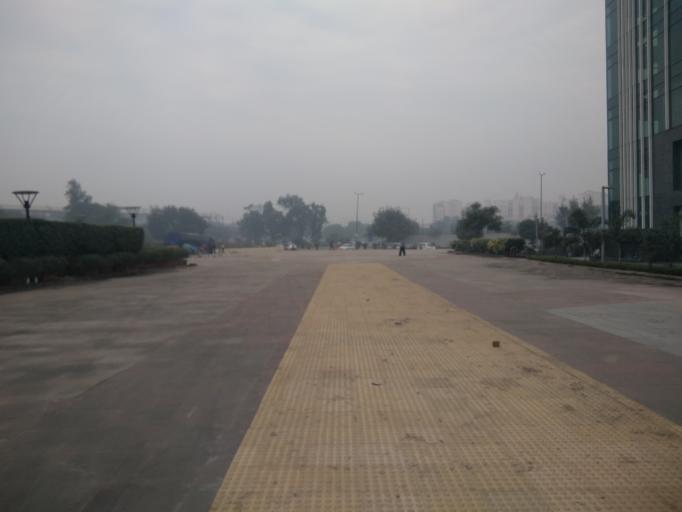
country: IN
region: Uttar Pradesh
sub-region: Gautam Buddha Nagar
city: Noida
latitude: 28.5381
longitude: 77.2867
